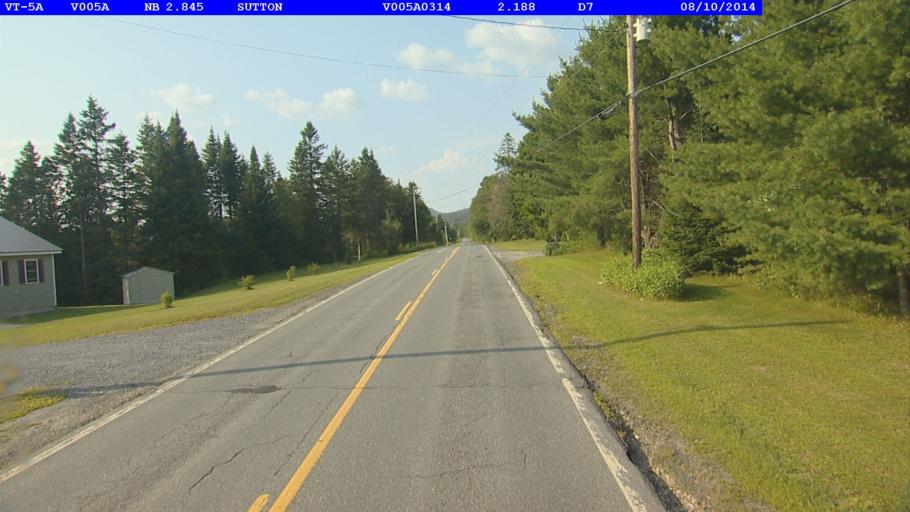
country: US
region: Vermont
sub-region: Caledonia County
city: Lyndonville
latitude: 44.6785
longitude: -71.9954
